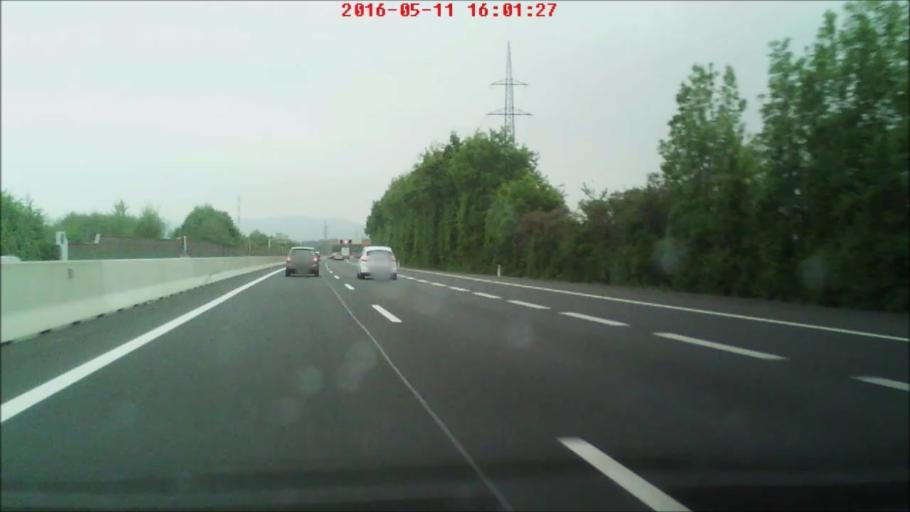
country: AT
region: Styria
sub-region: Politischer Bezirk Graz-Umgebung
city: Wundschuh
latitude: 46.9325
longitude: 15.4636
